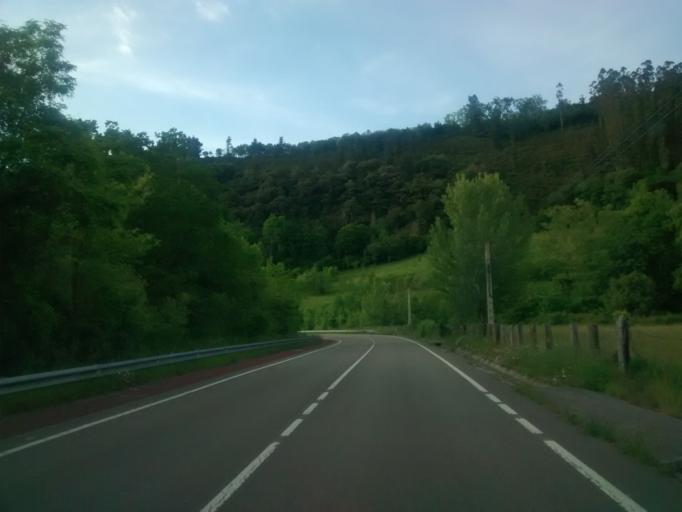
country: ES
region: Cantabria
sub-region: Provincia de Cantabria
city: San Vicente de la Barquera
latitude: 43.3034
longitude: -4.4627
